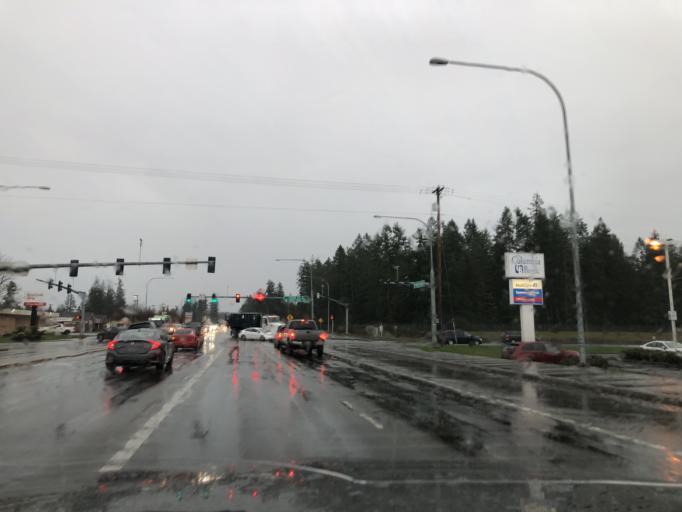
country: US
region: Washington
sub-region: Pierce County
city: Spanaway
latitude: 47.0980
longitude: -122.4350
